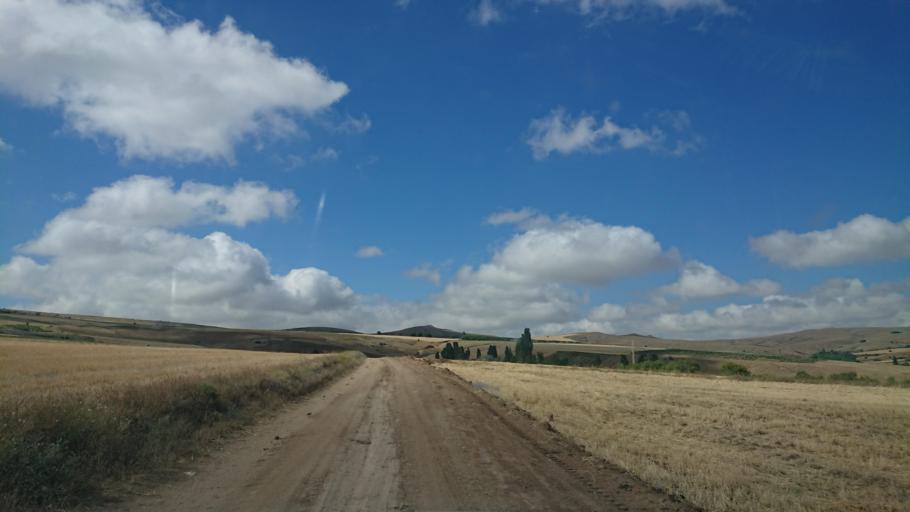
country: TR
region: Aksaray
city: Agacoren
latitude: 38.8528
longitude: 33.9398
